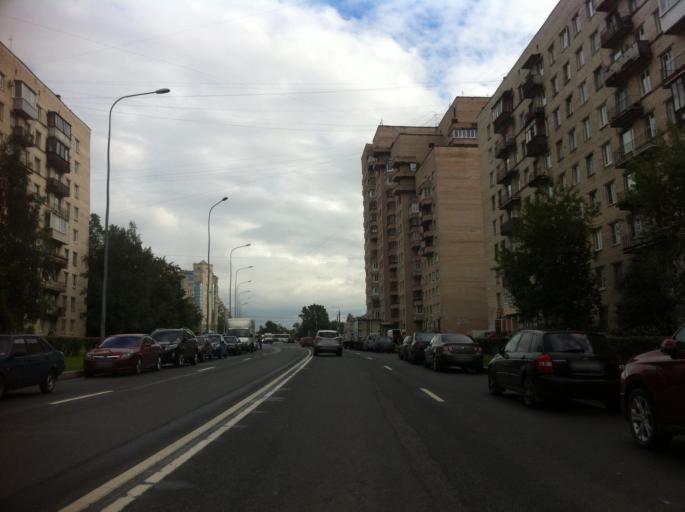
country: RU
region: St.-Petersburg
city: Dachnoye
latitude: 59.8418
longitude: 30.2356
